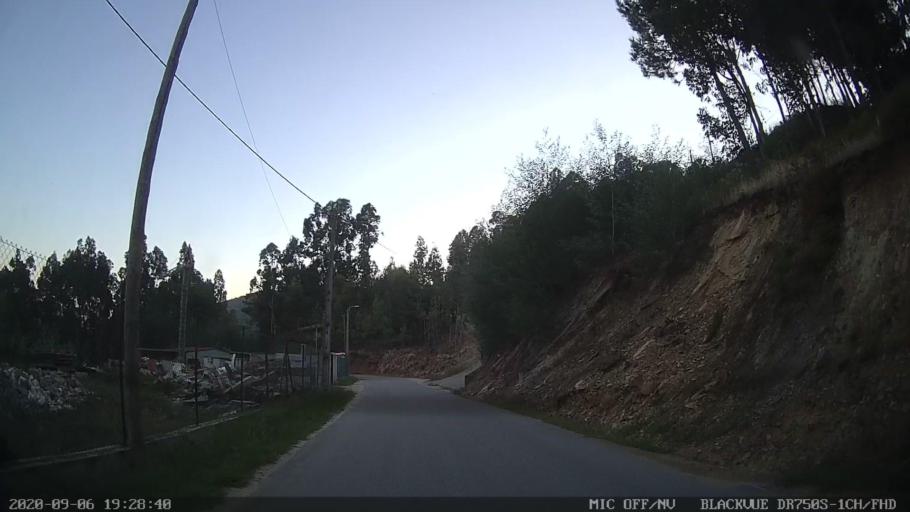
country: PT
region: Vila Real
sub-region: Mesao Frio
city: Mesao Frio
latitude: 41.1830
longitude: -7.9054
